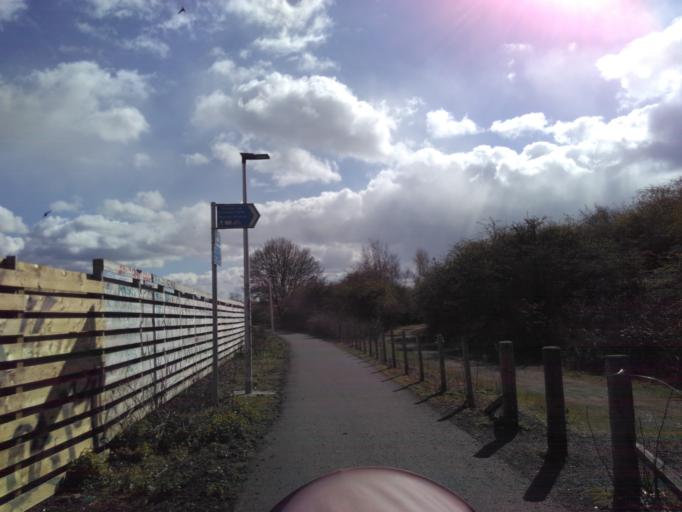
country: GB
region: Scotland
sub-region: Midlothian
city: Loanhead
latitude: 55.8888
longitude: -3.1470
